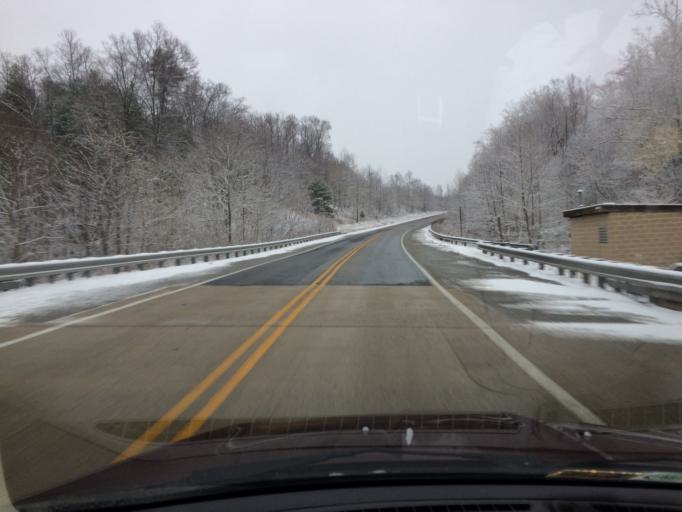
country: US
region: Virginia
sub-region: Amherst County
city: Amherst
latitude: 37.6587
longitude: -79.1450
